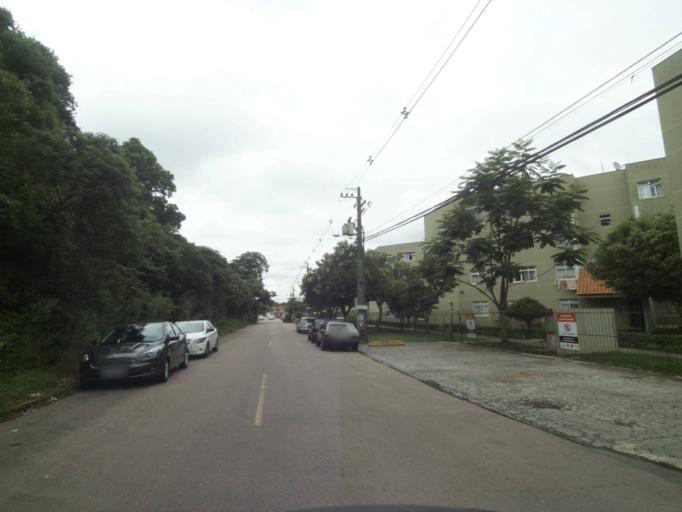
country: BR
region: Parana
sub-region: Curitiba
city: Curitiba
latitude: -25.4749
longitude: -49.3331
